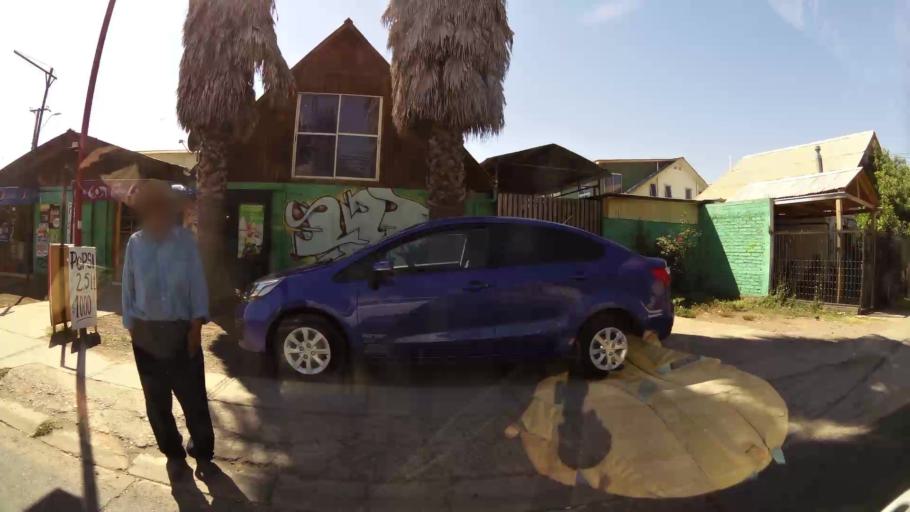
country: CL
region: Maule
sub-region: Provincia de Curico
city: Curico
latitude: -34.9667
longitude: -71.2409
